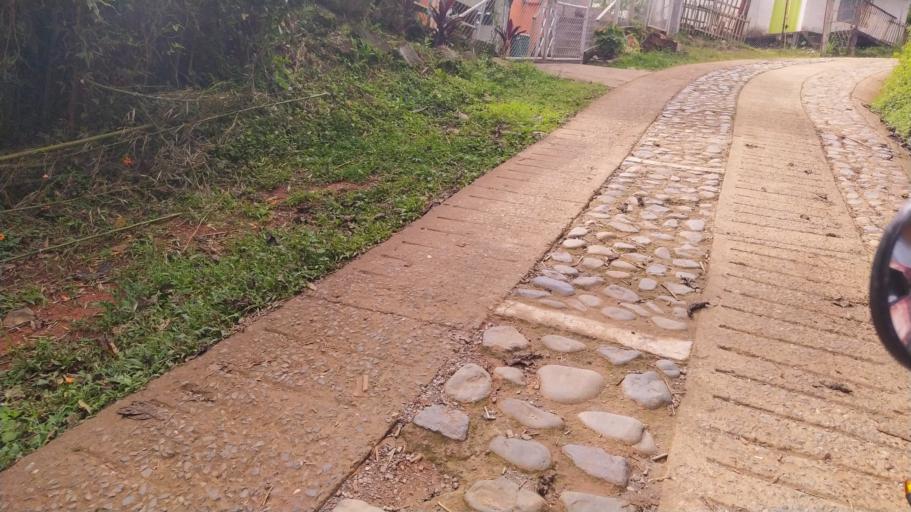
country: CO
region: Valle del Cauca
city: Cali
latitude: 3.4310
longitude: -76.6165
